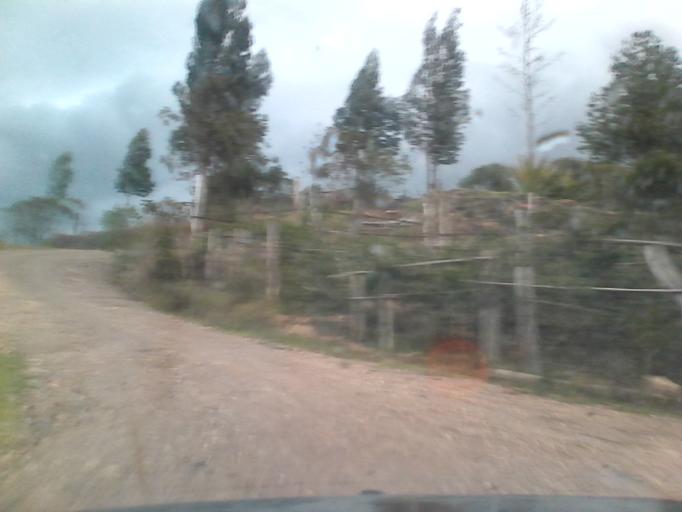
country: CO
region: Boyaca
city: Duitama
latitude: 5.8401
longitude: -73.0317
